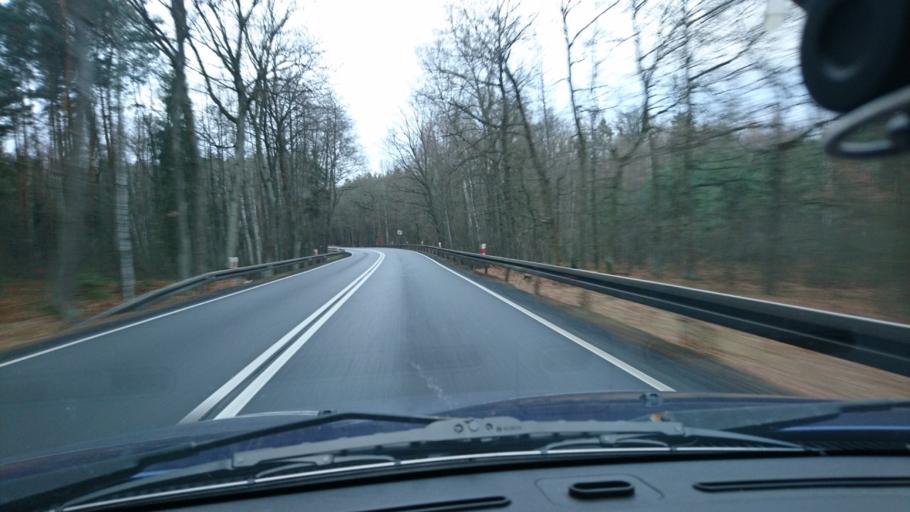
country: PL
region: Opole Voivodeship
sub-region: Powiat oleski
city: Olesno
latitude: 50.9360
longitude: 18.3306
